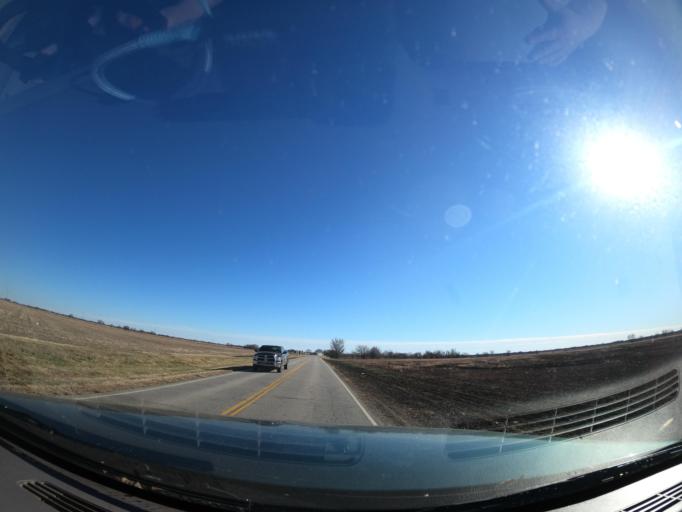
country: US
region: Oklahoma
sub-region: McIntosh County
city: Checotah
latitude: 35.5480
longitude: -95.6501
